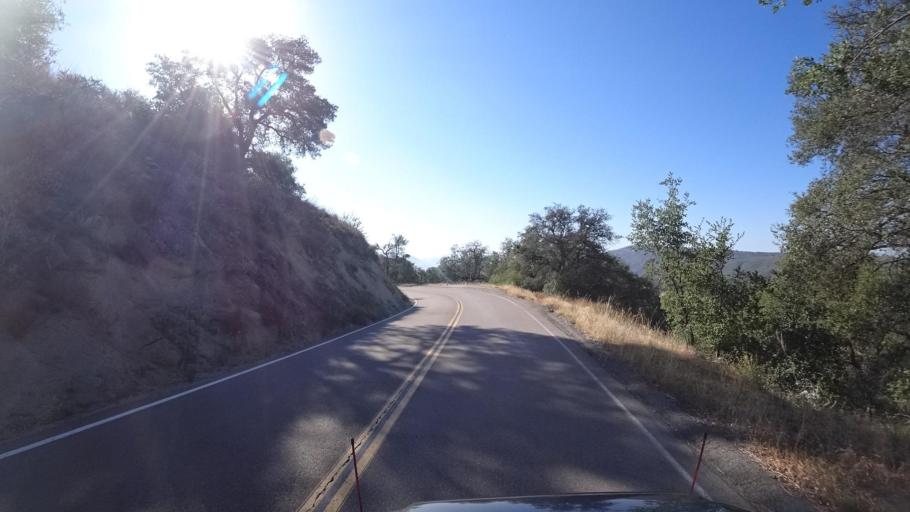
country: US
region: California
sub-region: Riverside County
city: Aguanga
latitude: 33.2678
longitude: -116.7803
